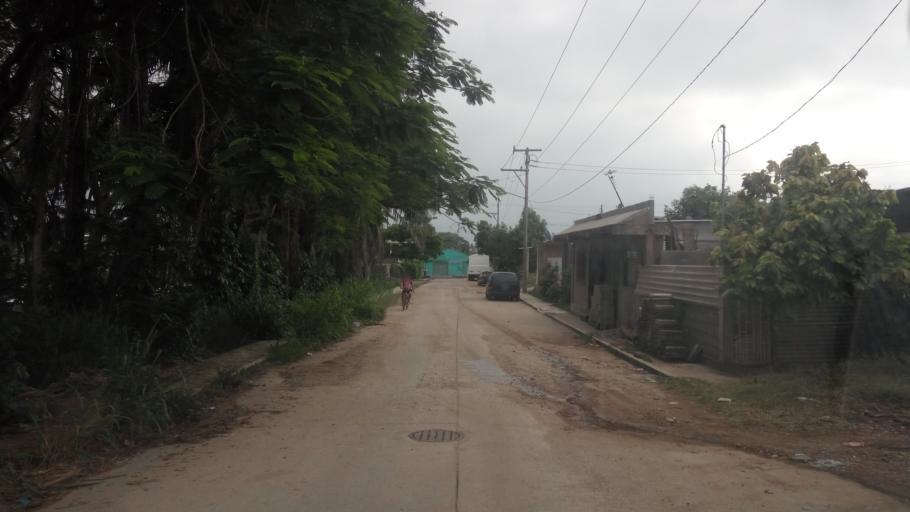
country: MX
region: Chiapas
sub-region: Reforma
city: El Carmen (El Limon)
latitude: 17.8537
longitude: -93.1555
